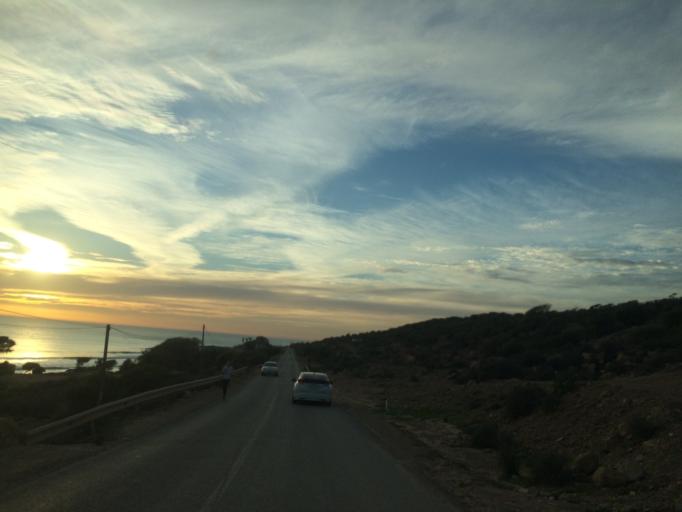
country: MA
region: Souss-Massa-Draa
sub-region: Agadir-Ida-ou-Tnan
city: Taghazout
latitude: 30.5473
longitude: -9.7174
